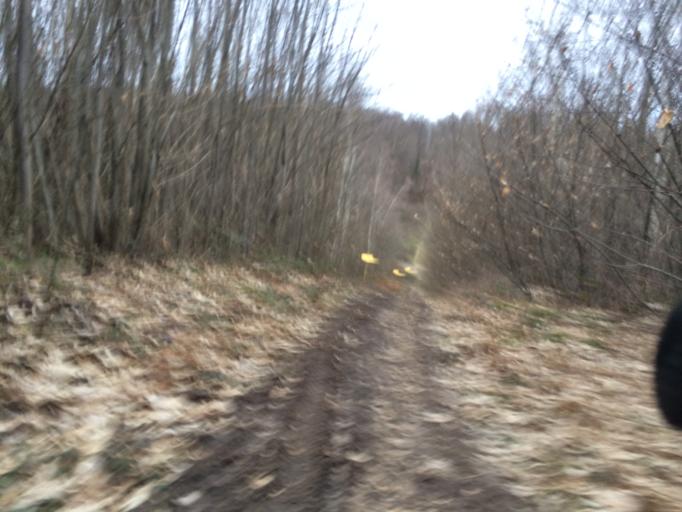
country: FR
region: Ile-de-France
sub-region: Departement de l'Essonne
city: Igny
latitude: 48.7428
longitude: 2.2161
